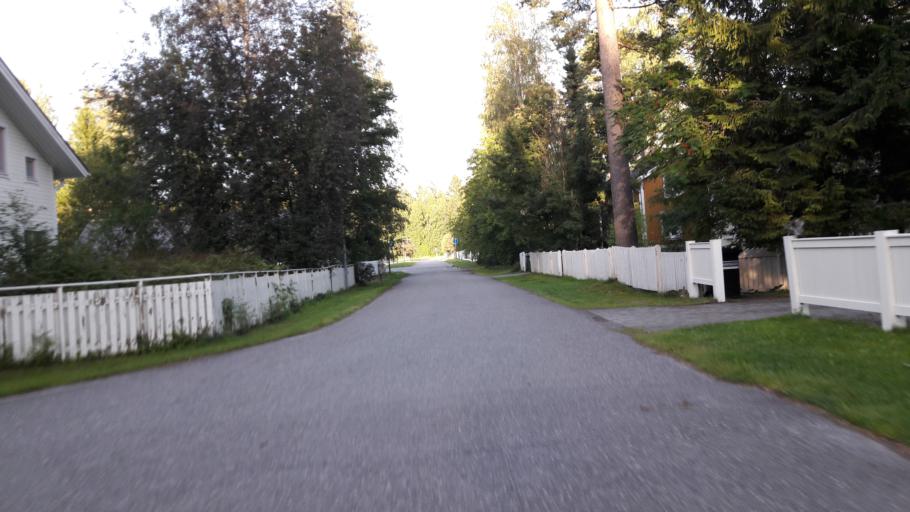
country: FI
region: North Karelia
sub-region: Joensuu
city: Joensuu
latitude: 62.6139
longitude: 29.7108
